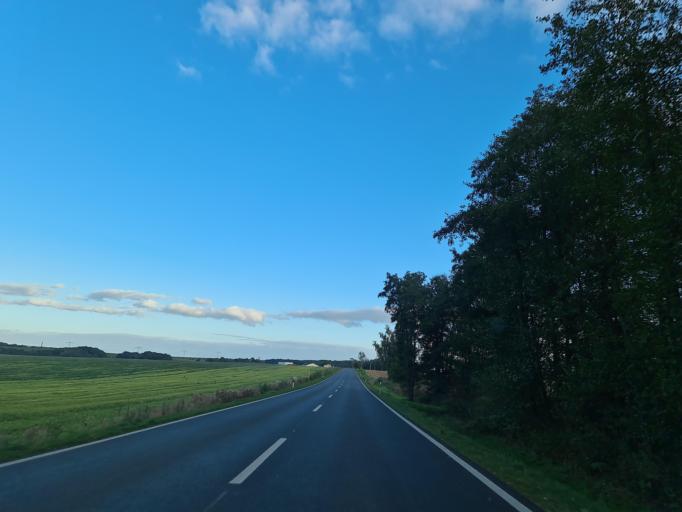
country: DE
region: Thuringia
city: Hohenolsen
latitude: 50.7350
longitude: 12.0929
